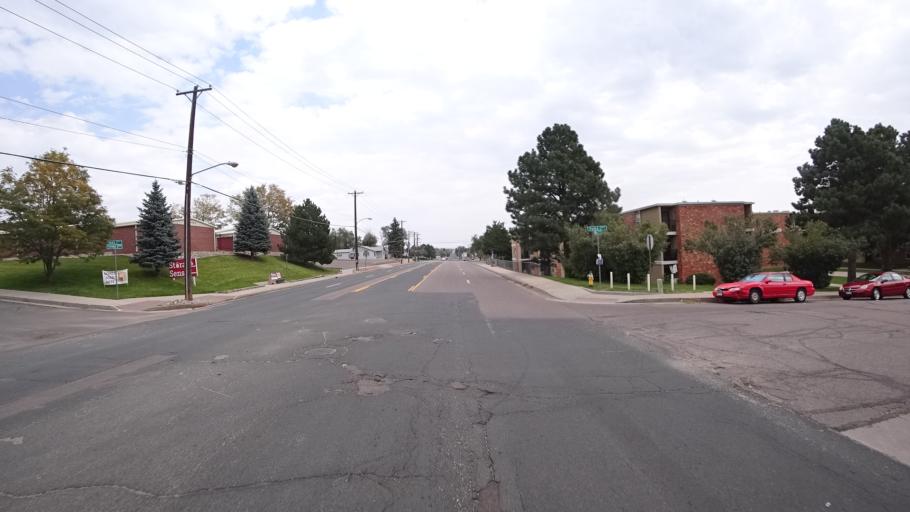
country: US
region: Colorado
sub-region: El Paso County
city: Colorado Springs
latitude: 38.8470
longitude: -104.7782
